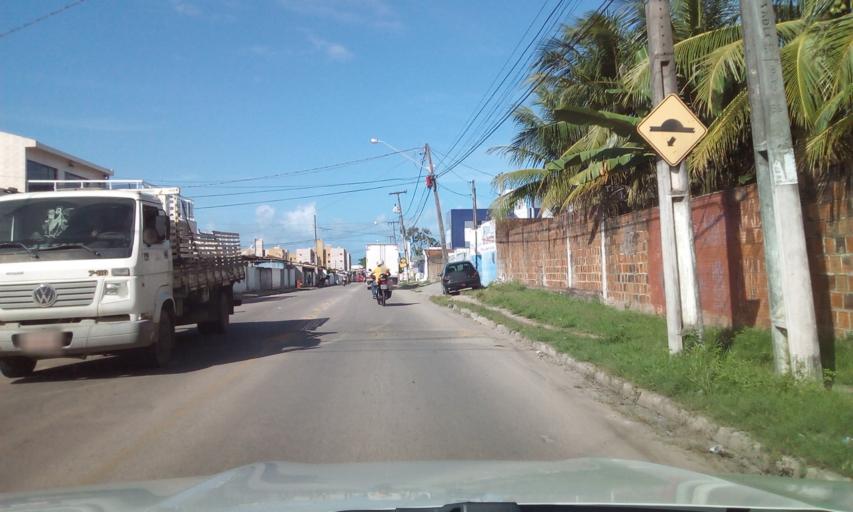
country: BR
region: Paraiba
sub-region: Joao Pessoa
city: Joao Pessoa
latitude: -7.1778
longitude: -34.8777
